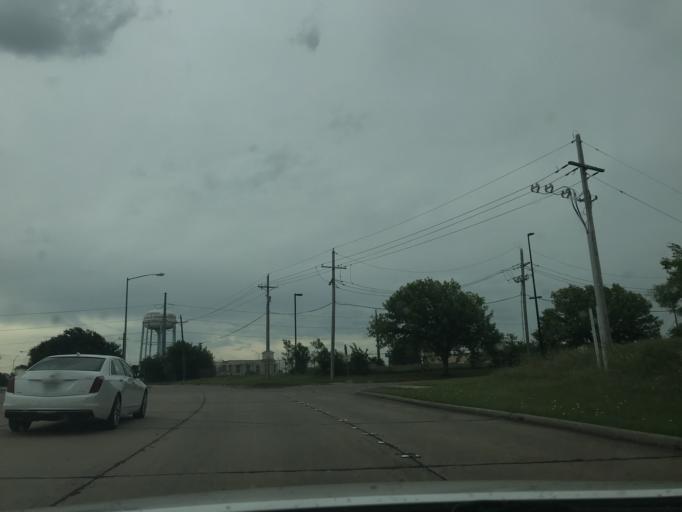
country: US
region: Texas
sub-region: Denton County
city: Lewisville
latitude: 33.0497
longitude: -97.0119
